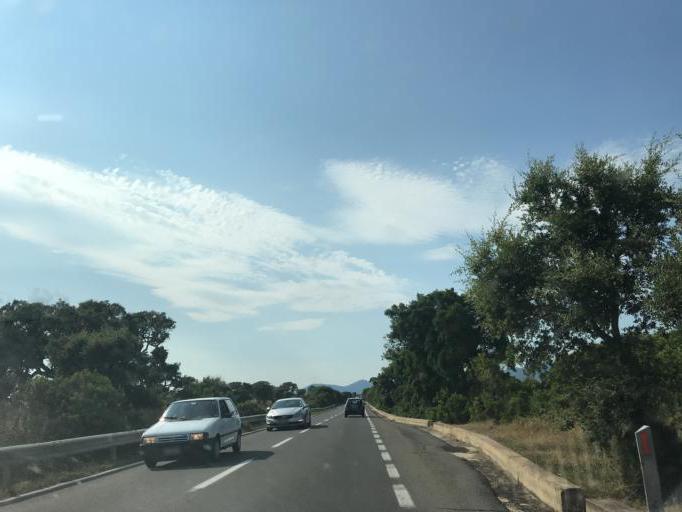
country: IT
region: Sardinia
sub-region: Provincia di Olbia-Tempio
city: Olbia
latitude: 40.8972
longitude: 9.5642
